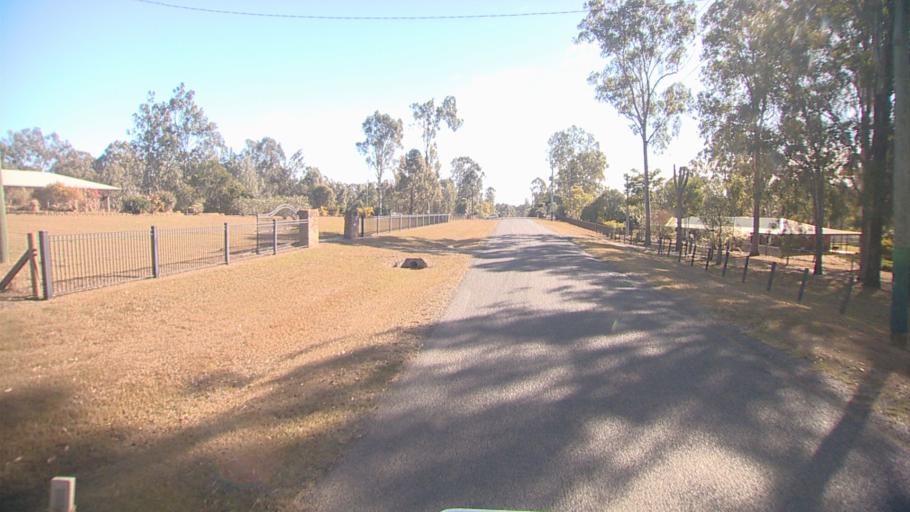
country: AU
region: Queensland
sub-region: Logan
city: Cedar Vale
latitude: -27.8753
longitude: 152.9848
